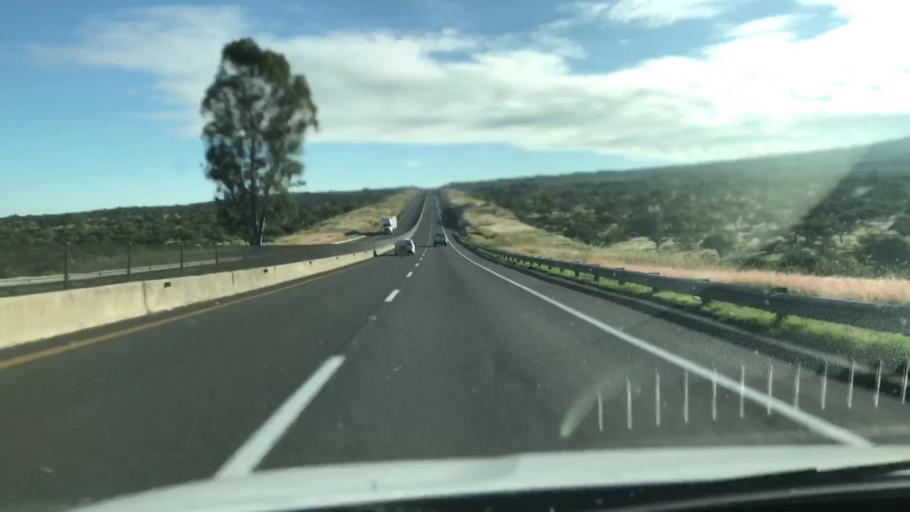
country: MX
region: Jalisco
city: Valle de Guadalupe
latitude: 21.0380
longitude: -102.5449
